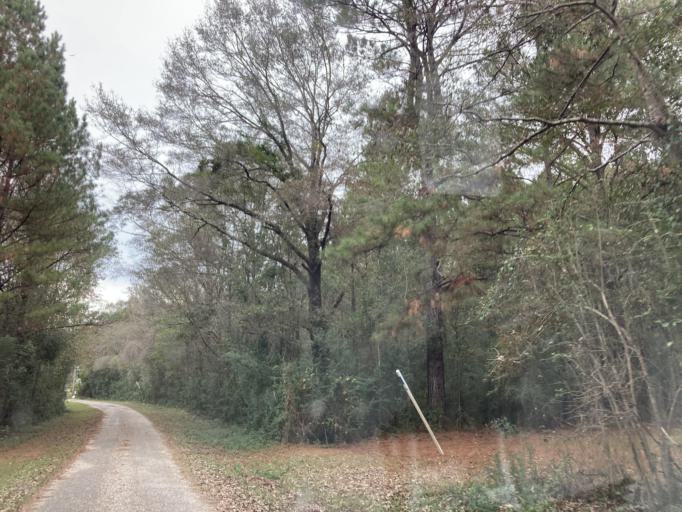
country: US
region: Mississippi
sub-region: Lamar County
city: Lumberton
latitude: 31.0338
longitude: -89.4590
